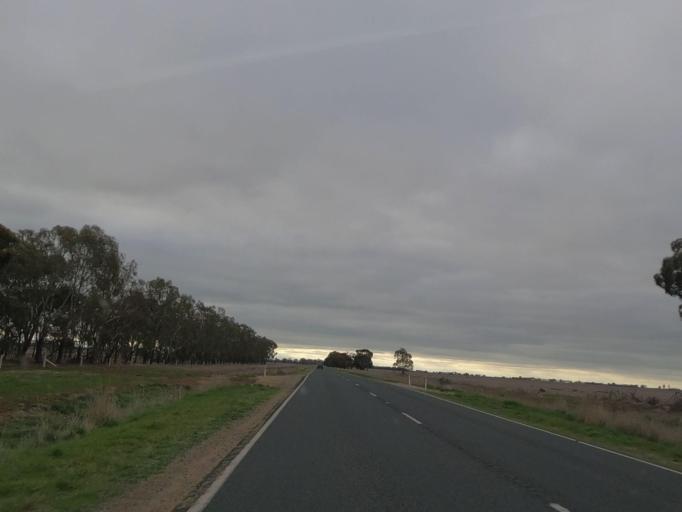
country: AU
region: Victoria
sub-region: Swan Hill
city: Swan Hill
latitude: -35.9708
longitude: 143.9438
